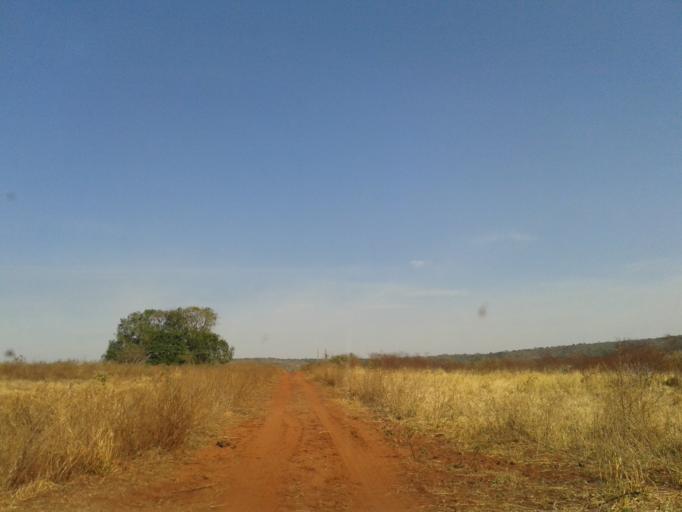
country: BR
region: Minas Gerais
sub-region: Santa Vitoria
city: Santa Vitoria
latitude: -19.2064
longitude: -50.0268
